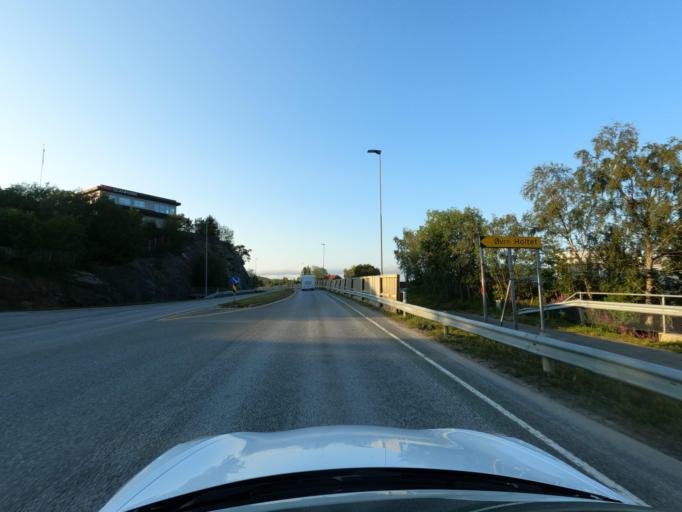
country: NO
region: Troms
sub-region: Harstad
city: Harstad
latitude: 68.7566
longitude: 16.5674
